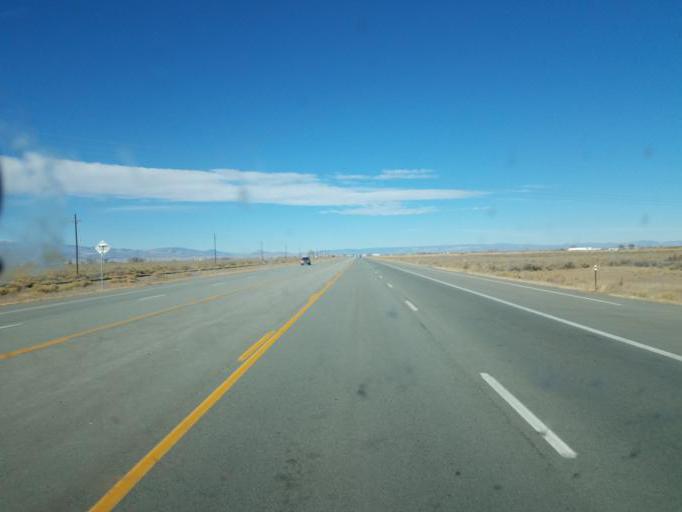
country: US
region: Colorado
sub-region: Alamosa County
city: Alamosa
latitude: 37.5207
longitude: -106.0019
